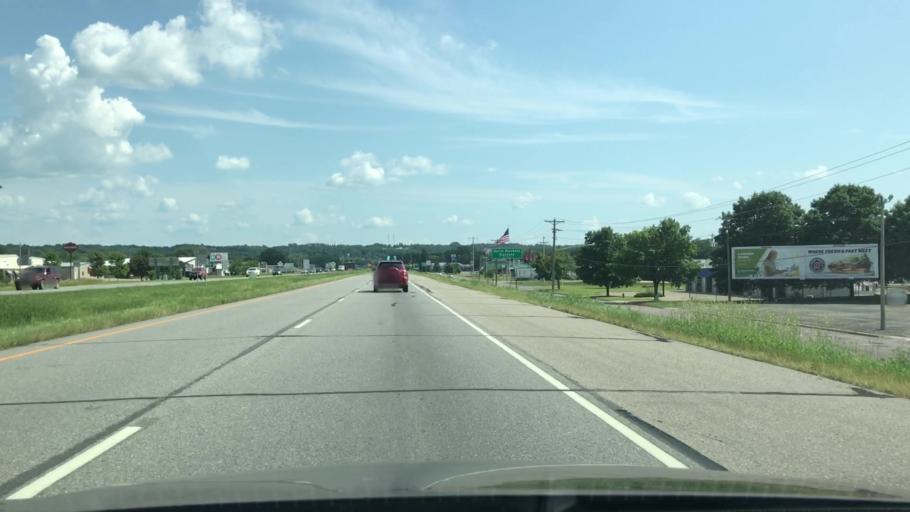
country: US
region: Minnesota
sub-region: Nicollet County
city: North Mankato
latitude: 44.1864
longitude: -94.0125
